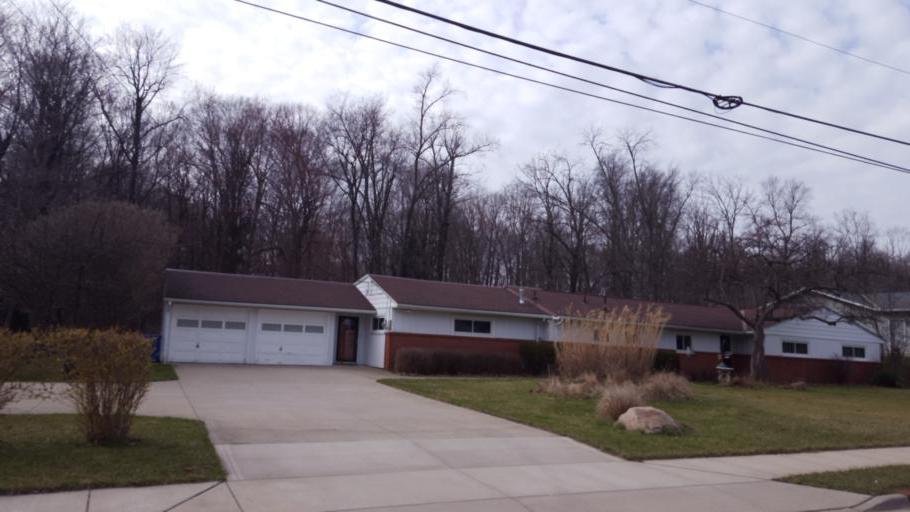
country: US
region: Ohio
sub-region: Richland County
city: Mansfield
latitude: 40.7193
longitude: -82.5388
